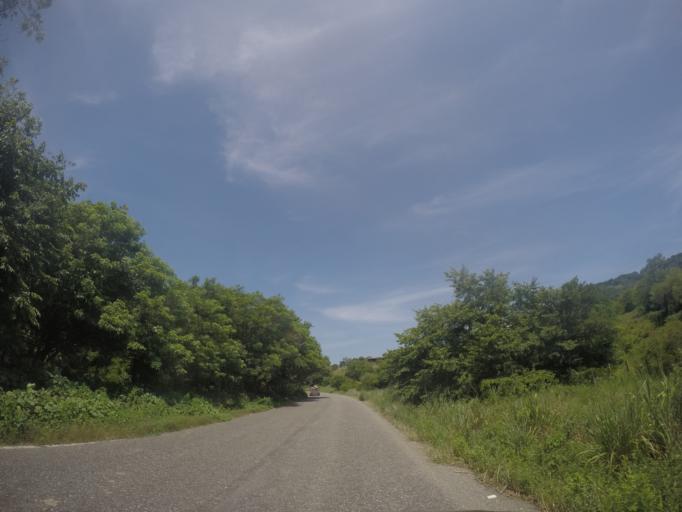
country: MX
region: Oaxaca
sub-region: Villa de Tututepec de Melchor Ocampo
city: Santa Rosa de Lima
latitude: 15.9924
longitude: -97.5365
